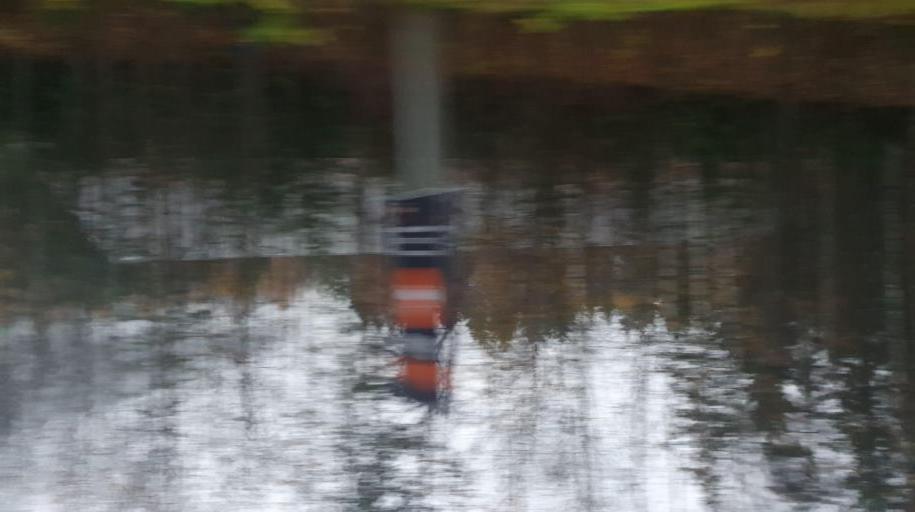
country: NO
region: Buskerud
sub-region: Krodsherad
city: Noresund
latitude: 60.1887
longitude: 9.6114
